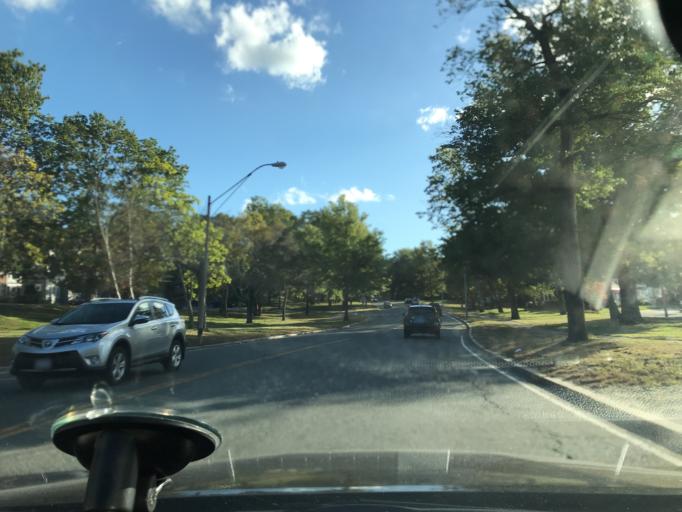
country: US
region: Massachusetts
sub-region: Suffolk County
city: Jamaica Plain
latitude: 42.2934
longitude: -71.1461
